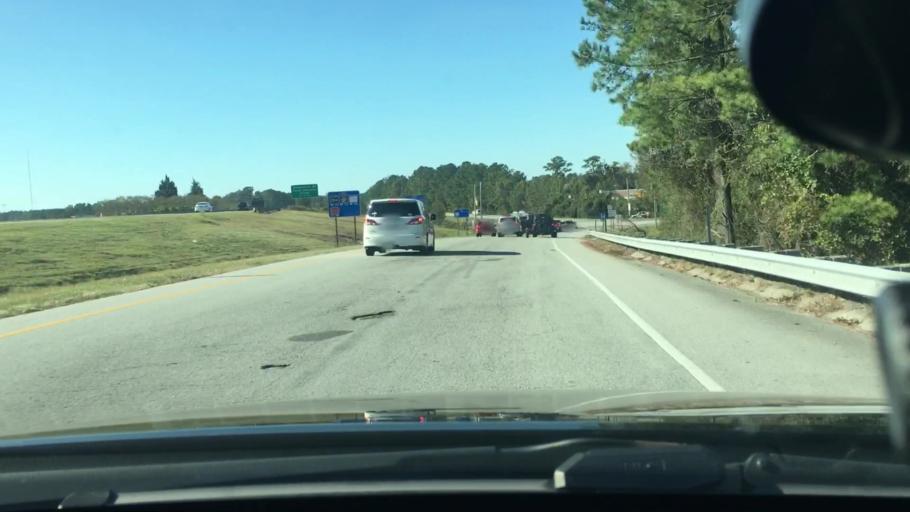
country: US
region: North Carolina
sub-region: Craven County
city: Trent Woods
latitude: 35.1029
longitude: -77.0821
